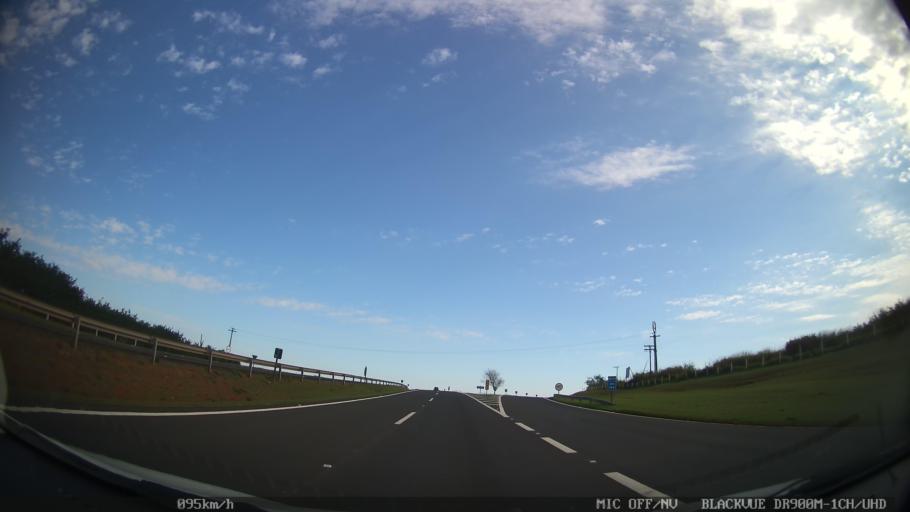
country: BR
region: Sao Paulo
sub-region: Iracemapolis
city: Iracemapolis
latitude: -22.6305
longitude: -47.5039
